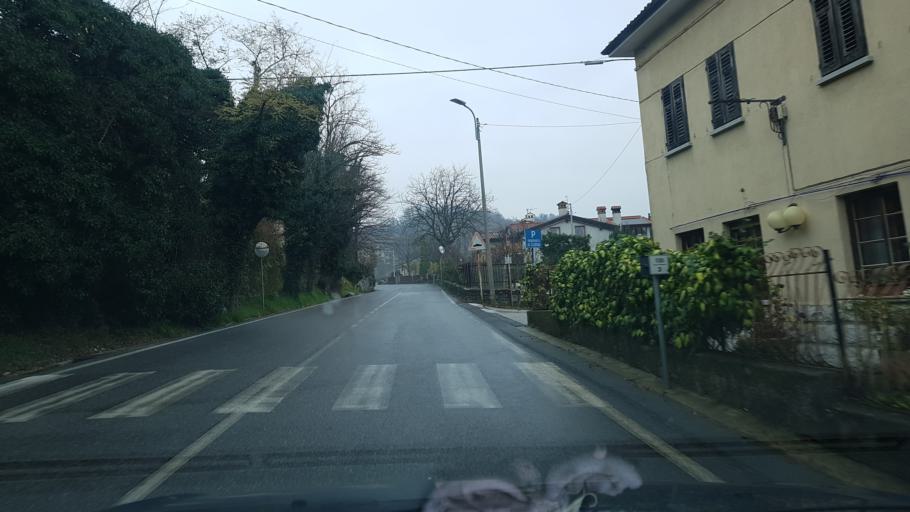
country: IT
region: Friuli Venezia Giulia
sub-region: Provincia di Trieste
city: Zolla
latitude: 45.7156
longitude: 13.8089
